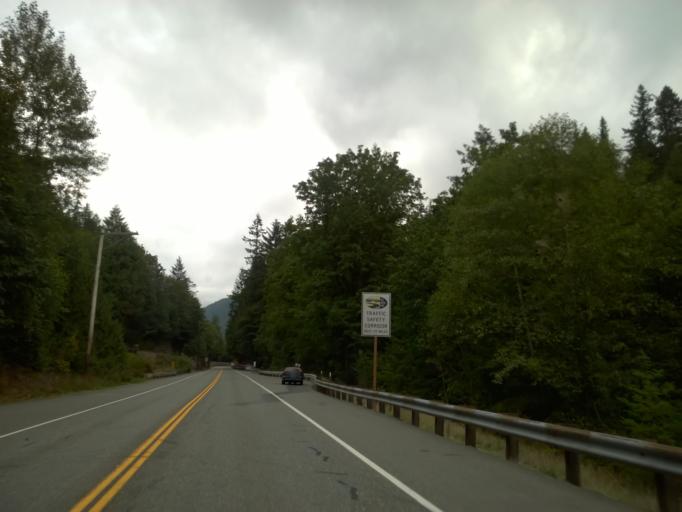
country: US
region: Washington
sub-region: Snohomish County
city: Gold Bar
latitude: 47.7975
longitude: -121.5147
